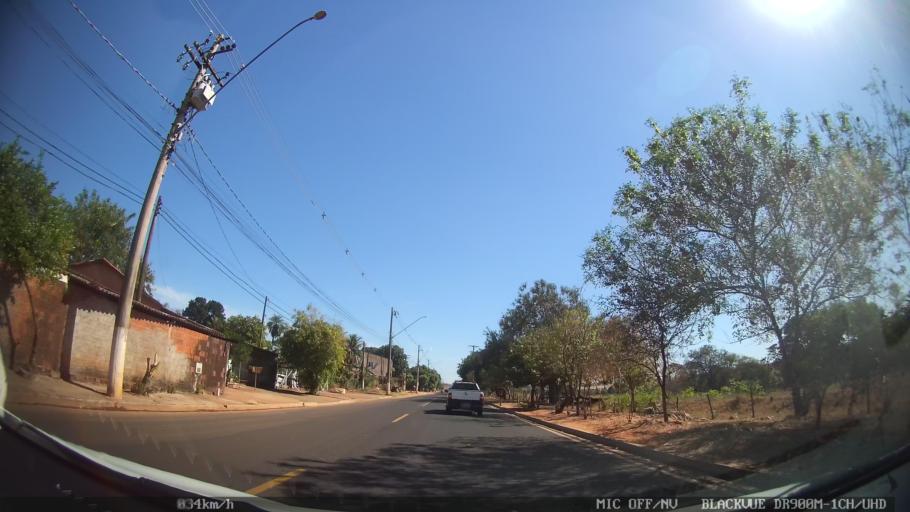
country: BR
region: Sao Paulo
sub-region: Sao Jose Do Rio Preto
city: Sao Jose do Rio Preto
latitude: -20.7616
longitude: -49.4309
